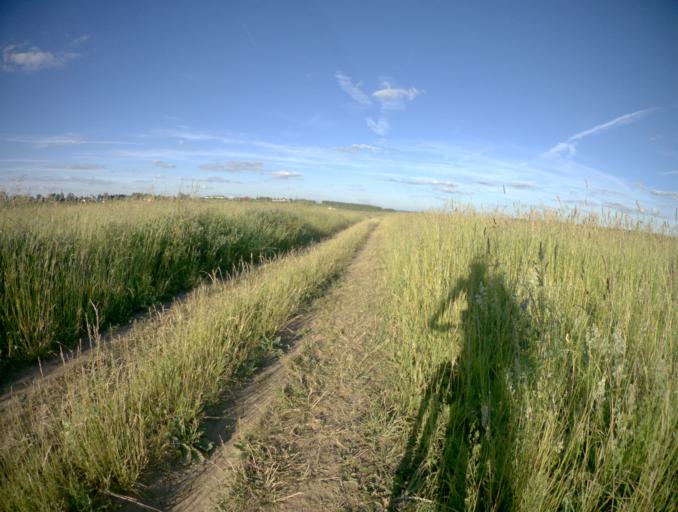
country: RU
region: Vladimir
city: Bogolyubovo
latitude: 56.1838
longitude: 40.4908
